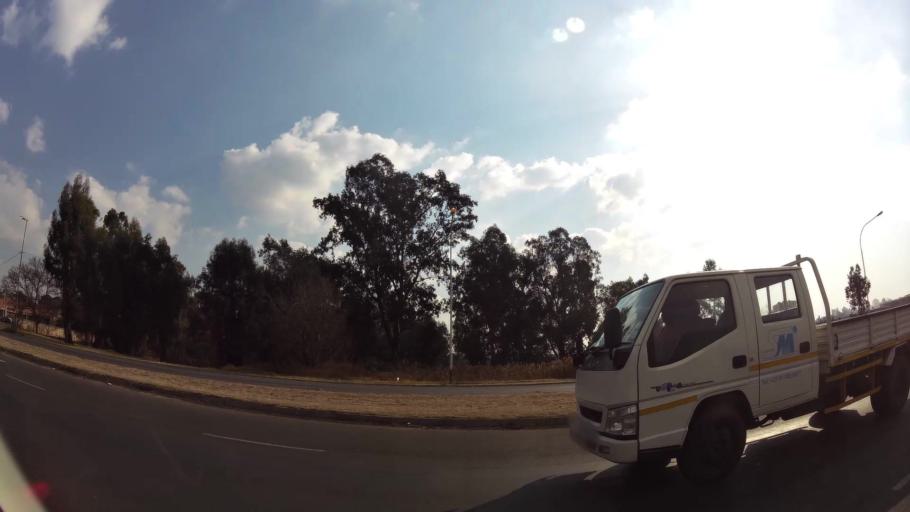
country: ZA
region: Gauteng
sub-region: Ekurhuleni Metropolitan Municipality
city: Boksburg
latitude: -26.2405
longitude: 28.2469
